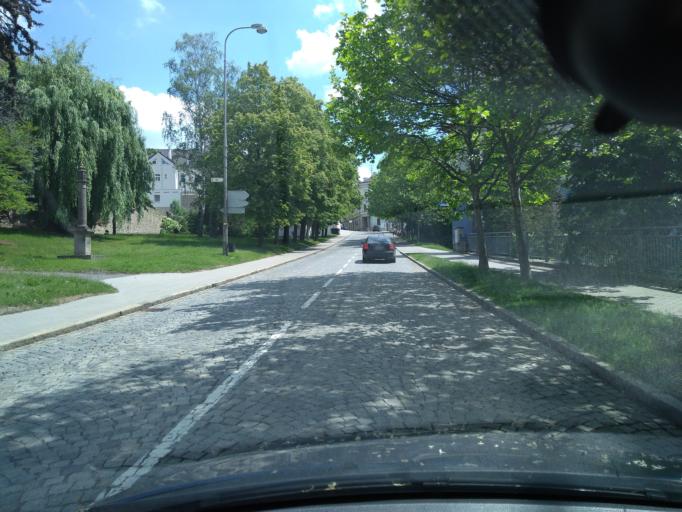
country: CZ
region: Plzensky
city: Klatovy
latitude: 49.3938
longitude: 13.2923
